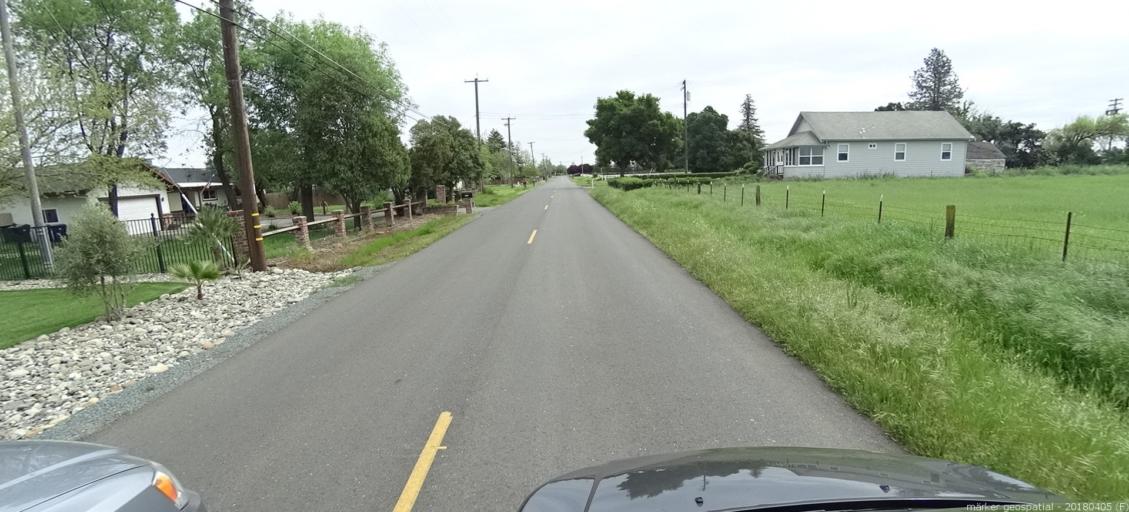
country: US
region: California
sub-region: Sacramento County
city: Galt
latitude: 38.2837
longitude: -121.3128
